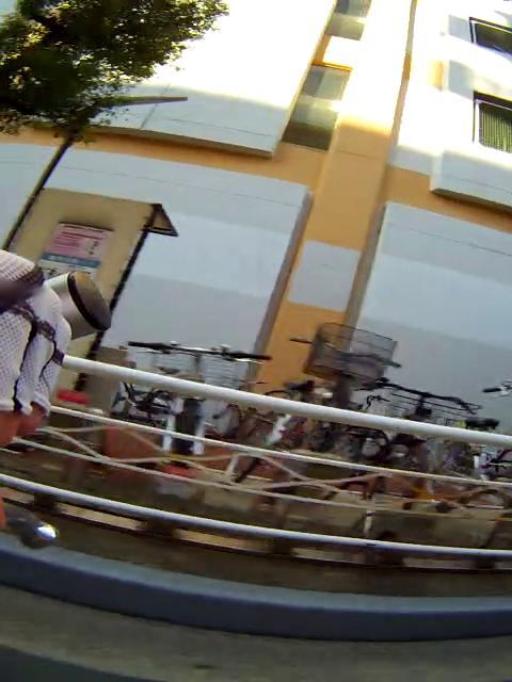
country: JP
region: Hyogo
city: Amagasaki
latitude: 34.7514
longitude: 135.4152
